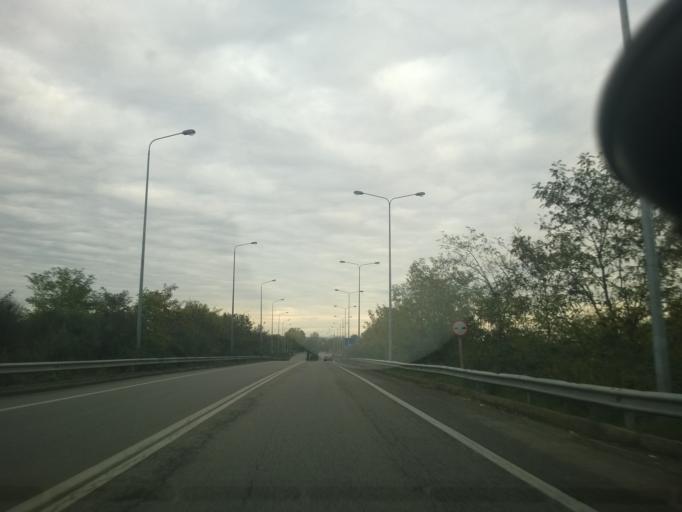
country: GR
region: Central Macedonia
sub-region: Nomos Pellis
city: Melissi
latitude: 40.7778
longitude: 22.3616
